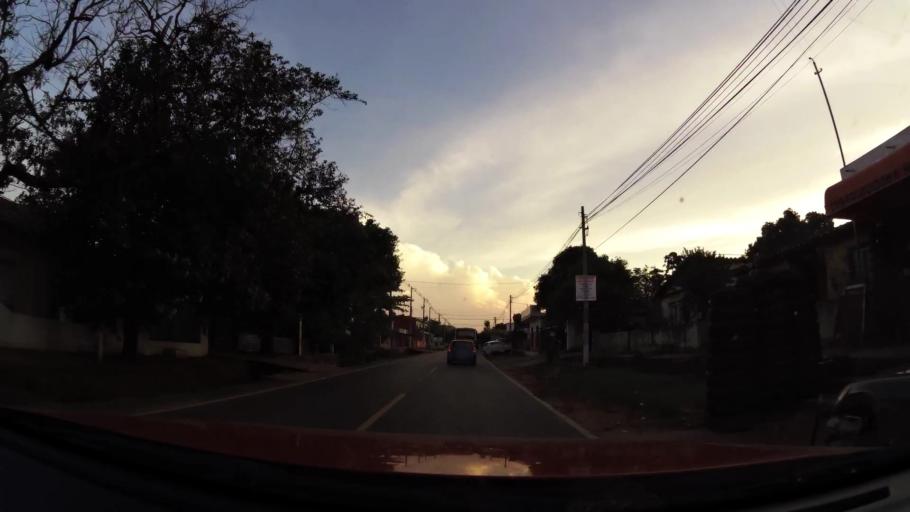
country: PY
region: Central
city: San Lorenzo
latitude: -25.3766
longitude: -57.4925
